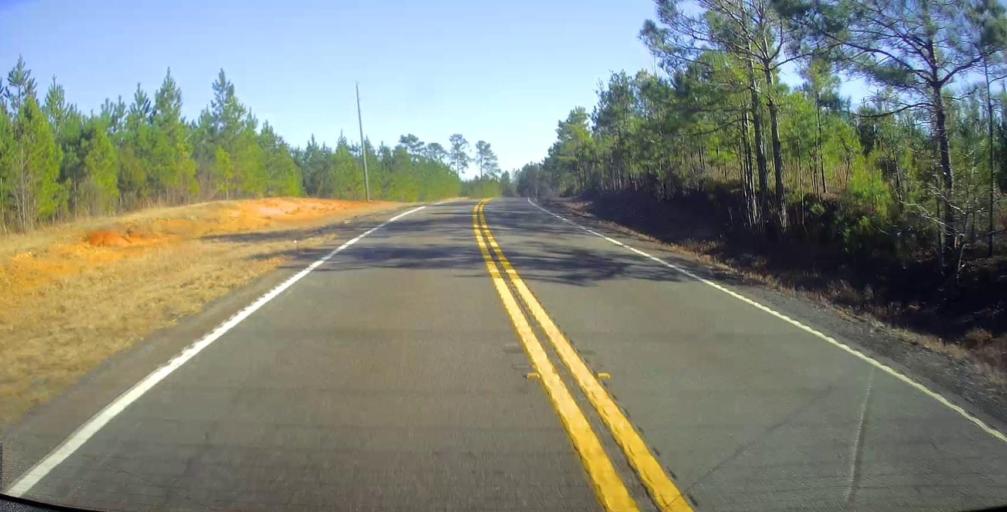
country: US
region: Georgia
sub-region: Talbot County
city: Talbotton
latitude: 32.6495
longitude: -84.3897
